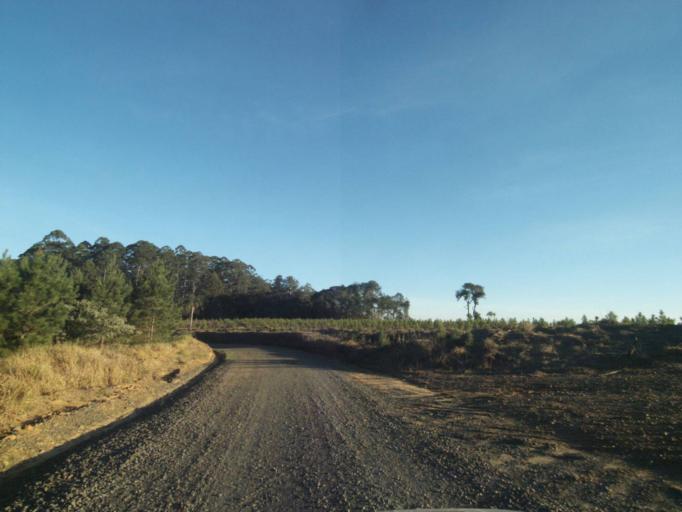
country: BR
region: Parana
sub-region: Telemaco Borba
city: Telemaco Borba
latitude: -24.4555
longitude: -50.6017
